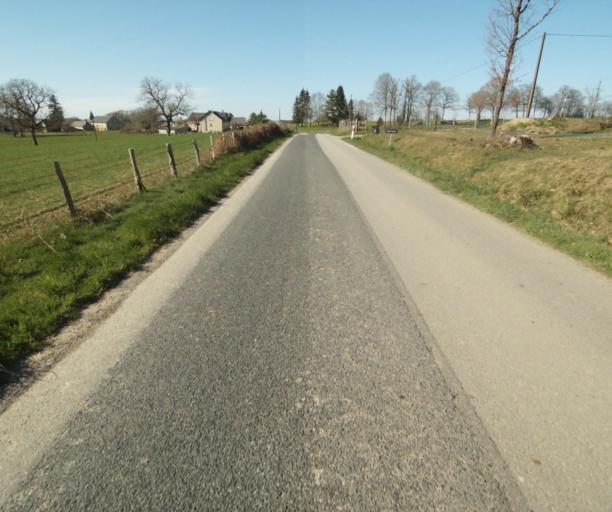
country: FR
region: Limousin
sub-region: Departement de la Correze
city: Chamboulive
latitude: 45.4836
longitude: 1.7133
